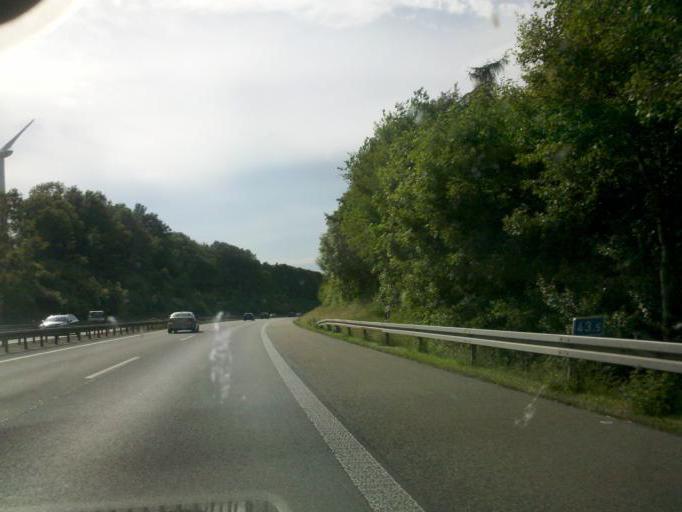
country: DE
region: North Rhine-Westphalia
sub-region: Regierungsbezirk Arnsberg
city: Nachrodt-Wiblingwerde
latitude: 51.2893
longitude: 7.5631
